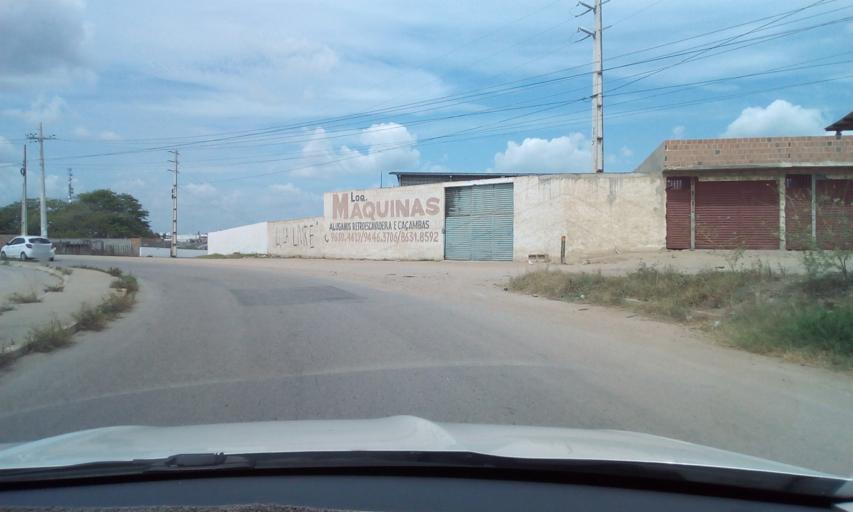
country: BR
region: Pernambuco
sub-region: Bezerros
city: Bezerros
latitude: -8.2482
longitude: -35.7582
